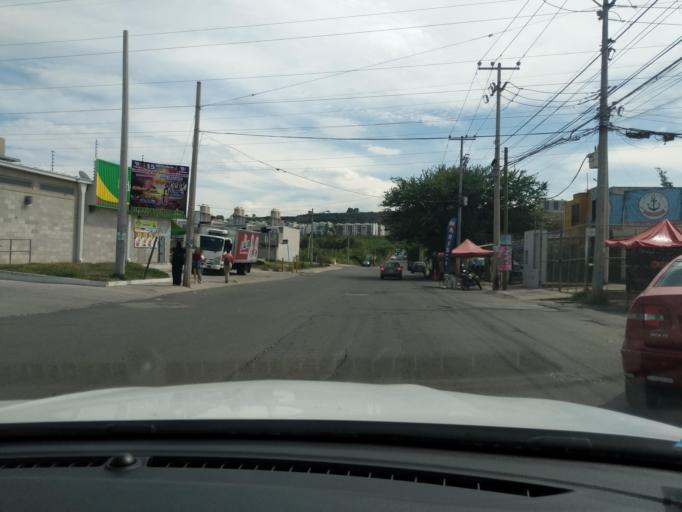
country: MX
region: Jalisco
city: Tonala
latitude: 20.6452
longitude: -103.2274
